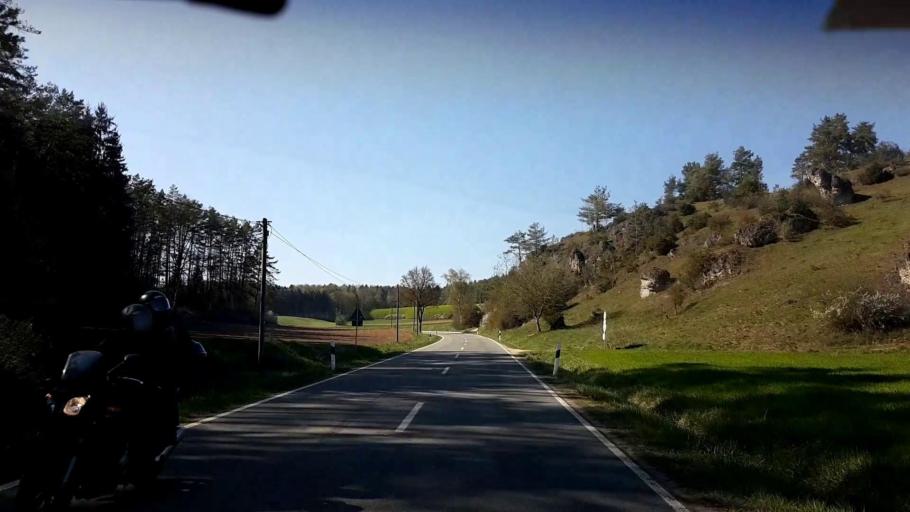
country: DE
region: Bavaria
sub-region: Upper Franconia
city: Pottenstein
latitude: 49.7891
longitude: 11.4210
